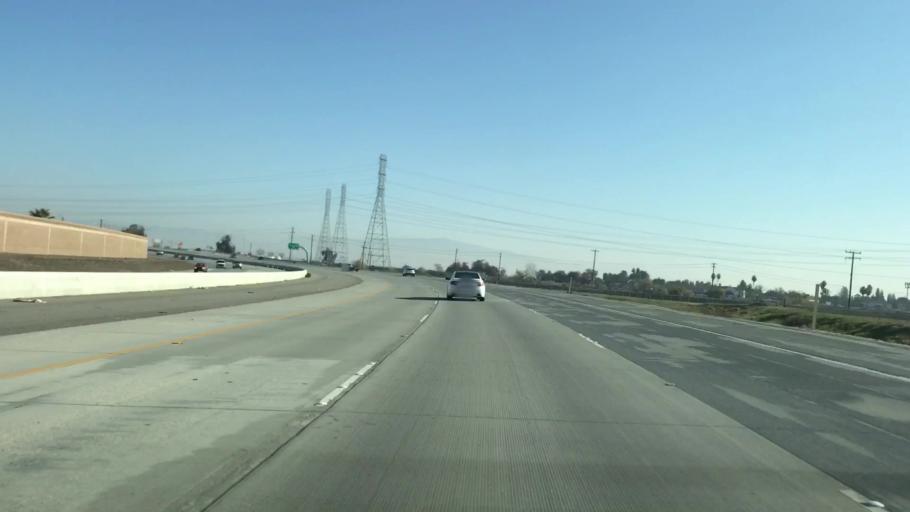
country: US
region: California
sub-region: Kern County
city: Greenacres
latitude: 35.3617
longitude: -119.0995
